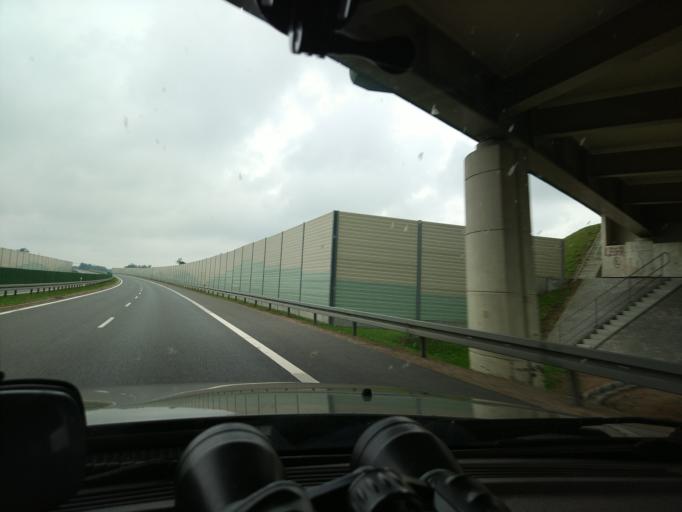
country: PL
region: Podlasie
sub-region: Powiat zambrowski
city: Zambrow
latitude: 53.0117
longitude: 22.3041
